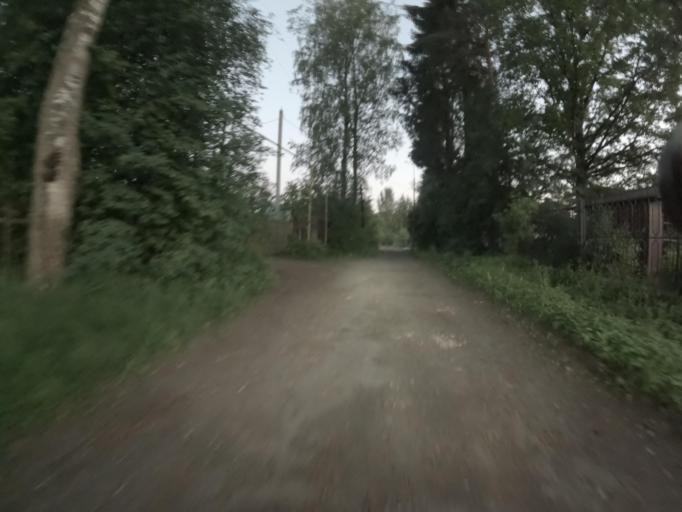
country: RU
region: Leningrad
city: Vsevolozhsk
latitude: 60.0124
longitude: 30.6041
